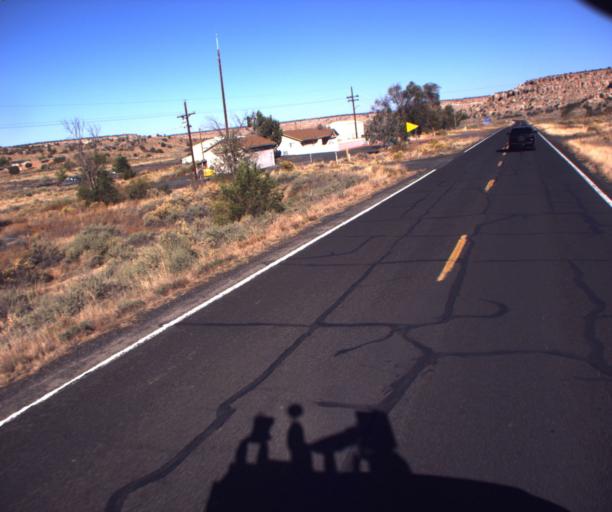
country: US
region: Arizona
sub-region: Navajo County
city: First Mesa
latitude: 35.8228
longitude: -110.2192
